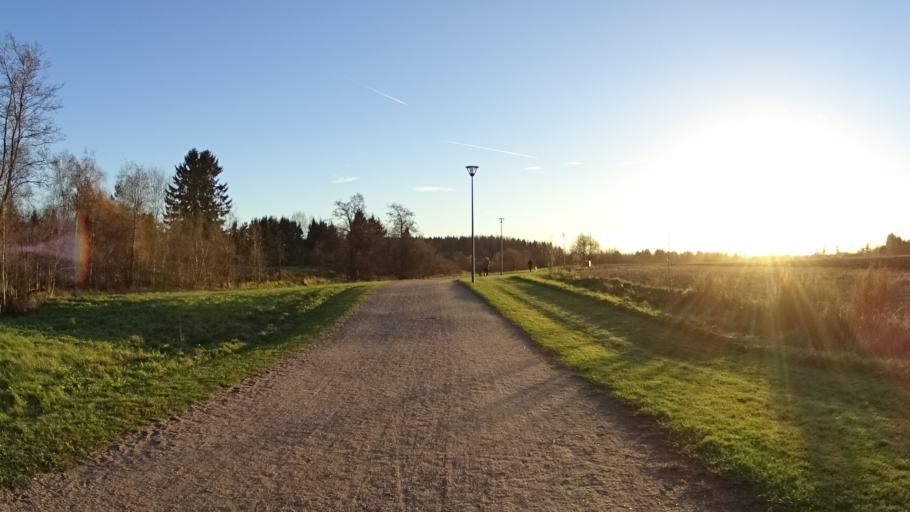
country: FI
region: Uusimaa
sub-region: Helsinki
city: Vantaa
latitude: 60.2848
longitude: 24.9988
